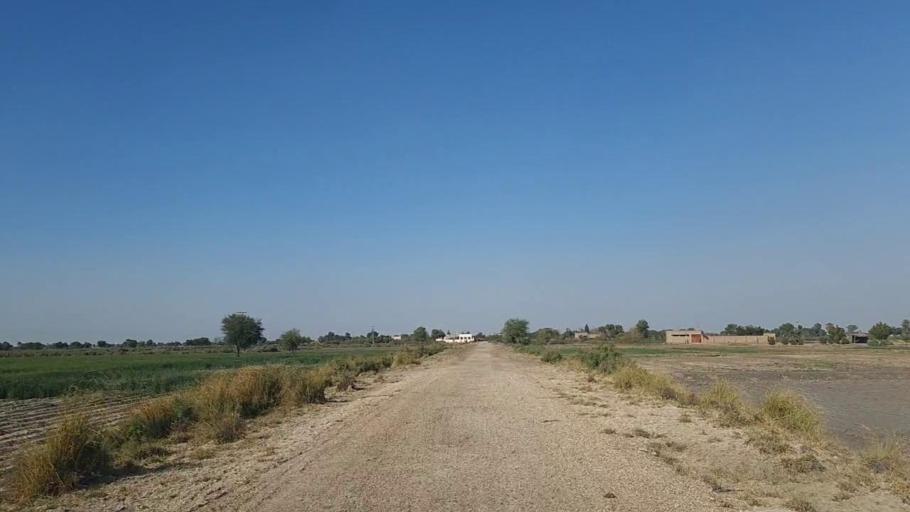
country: PK
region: Sindh
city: Shahpur Chakar
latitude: 26.2190
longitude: 68.6347
